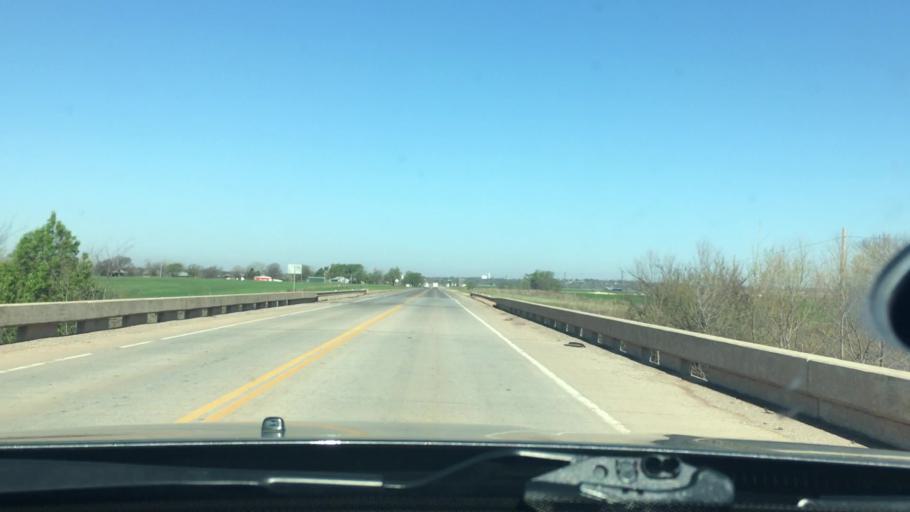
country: US
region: Oklahoma
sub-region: Garvin County
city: Lindsay
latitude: 34.8310
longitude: -97.5738
